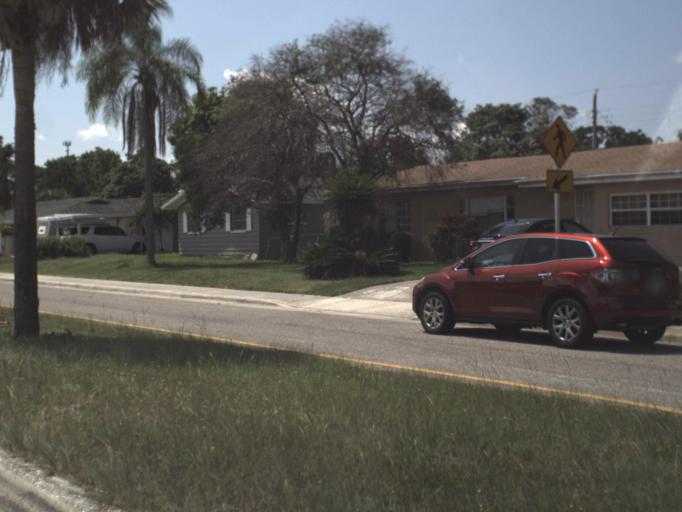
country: US
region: Florida
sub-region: Pinellas County
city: Kenneth City
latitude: 27.7863
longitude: -82.7211
